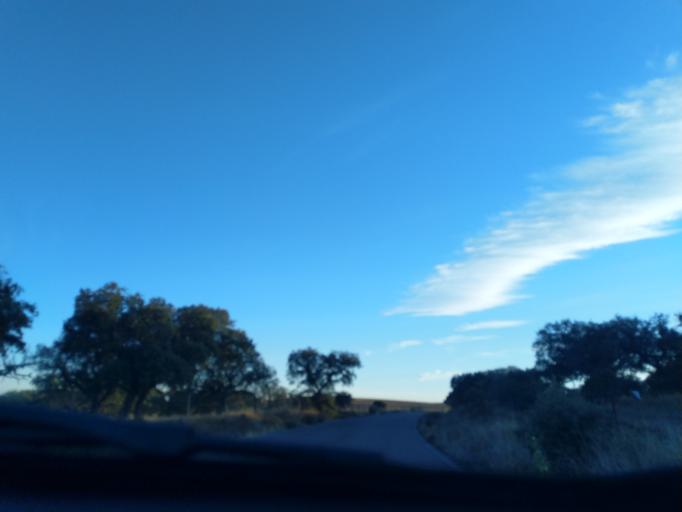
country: ES
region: Extremadura
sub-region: Provincia de Badajoz
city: Valverde de Llerena
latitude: 38.2334
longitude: -5.8223
